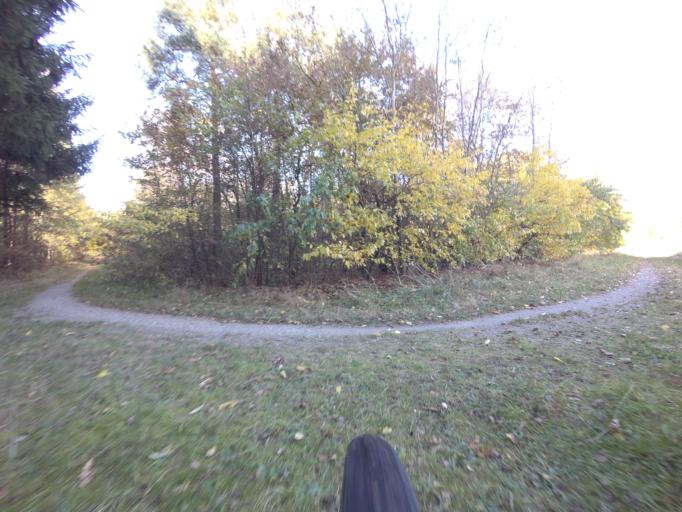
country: DK
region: Central Jutland
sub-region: Syddjurs Kommune
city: Ryomgard
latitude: 56.4168
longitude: 10.5676
